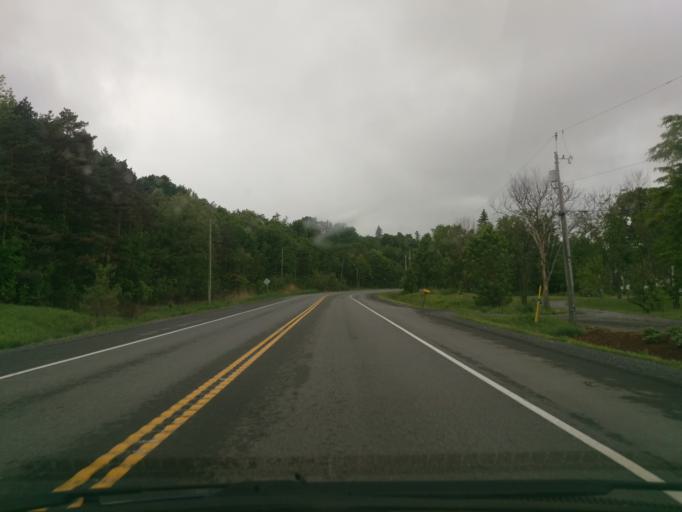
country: CA
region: Ontario
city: Clarence-Rockland
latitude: 45.5154
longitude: -75.4500
